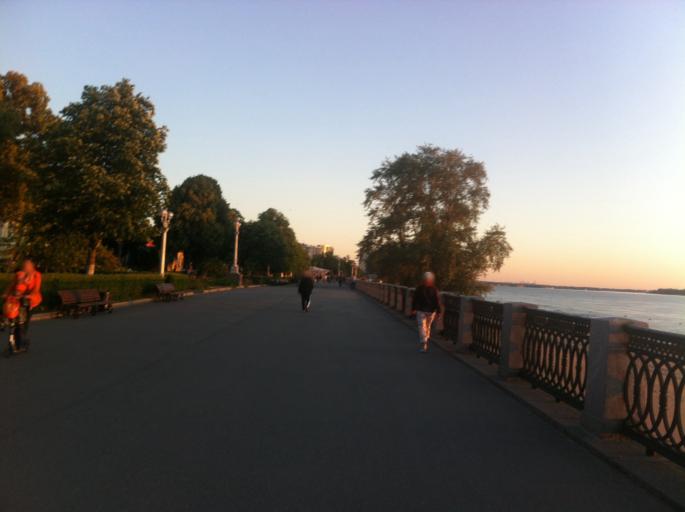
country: RU
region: Samara
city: Rozhdestveno
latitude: 53.1935
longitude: 50.0869
